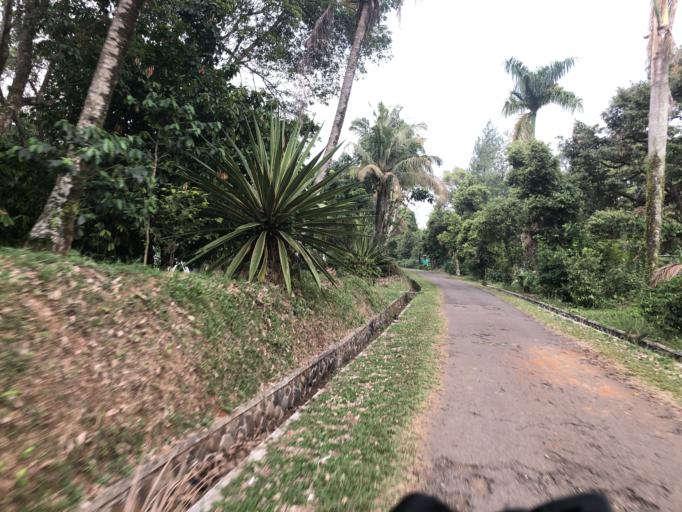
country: ID
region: West Java
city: Ciampea
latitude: -6.5524
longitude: 106.7175
